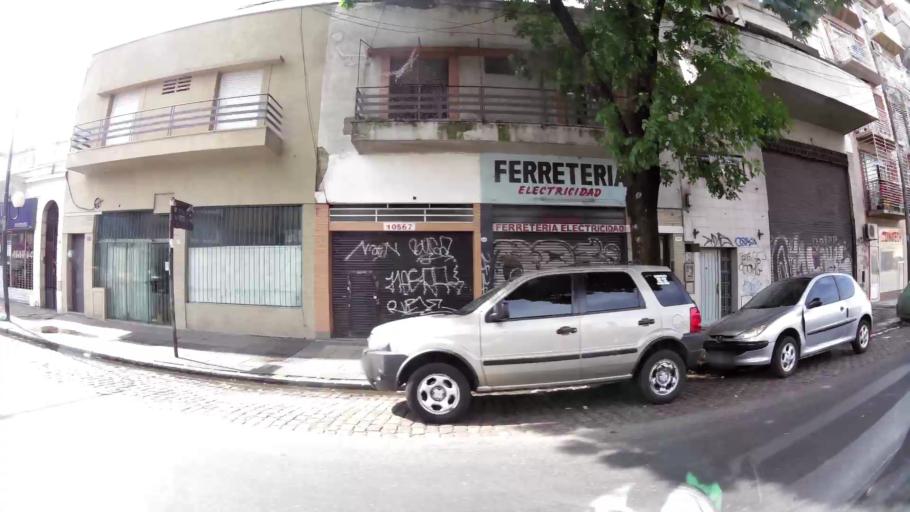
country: AR
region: Buenos Aires F.D.
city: Villa Santa Rita
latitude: -34.6392
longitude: -58.5126
